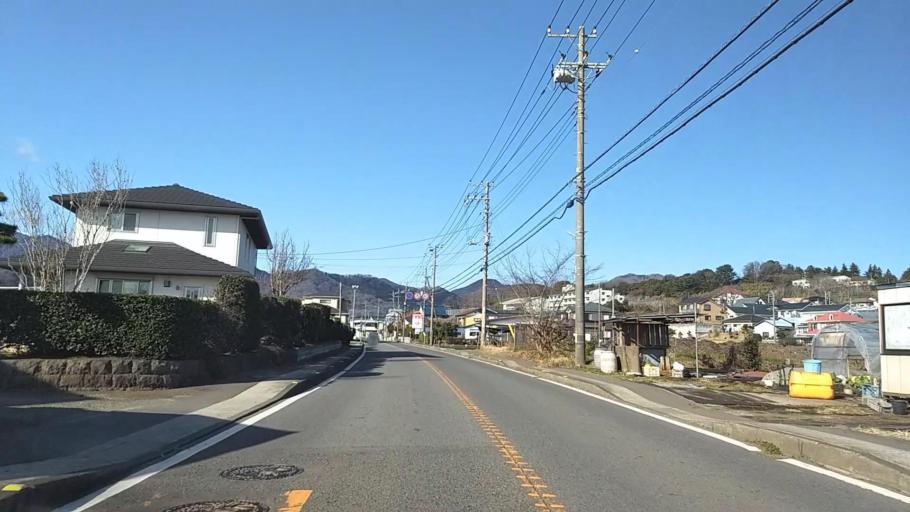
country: JP
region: Kanagawa
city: Atsugi
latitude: 35.4703
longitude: 139.3246
